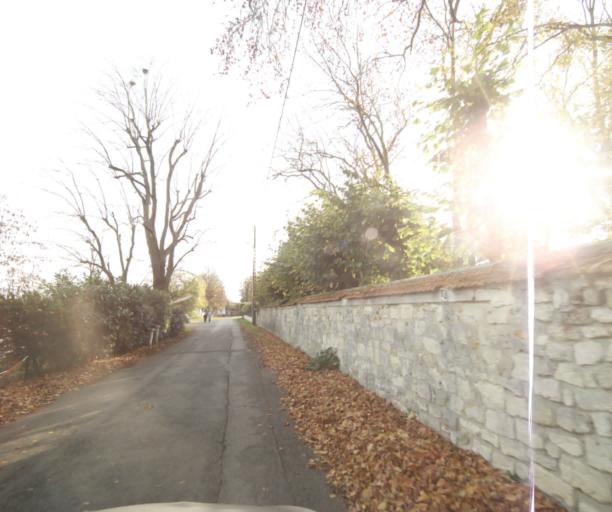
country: FR
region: Ile-de-France
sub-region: Departement des Yvelines
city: Conflans-Sainte-Honorine
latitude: 48.9802
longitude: 2.1012
